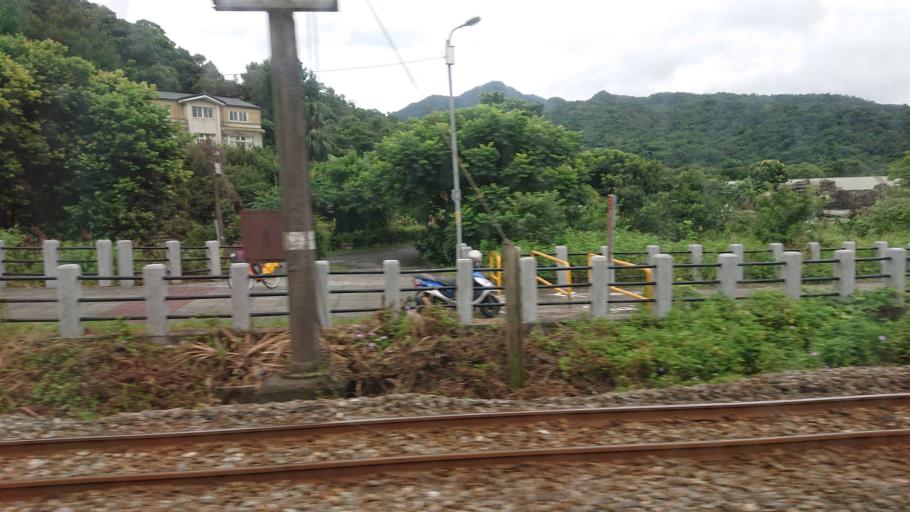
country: TW
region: Taiwan
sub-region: Keelung
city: Keelung
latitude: 25.1055
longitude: 121.8265
